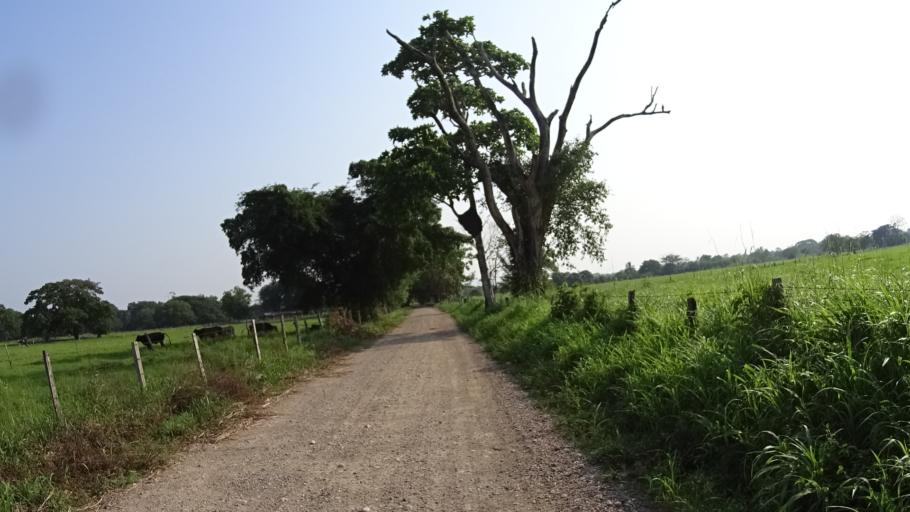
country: CO
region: Cundinamarca
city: Puerto Salgar
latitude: 5.5454
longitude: -74.6712
